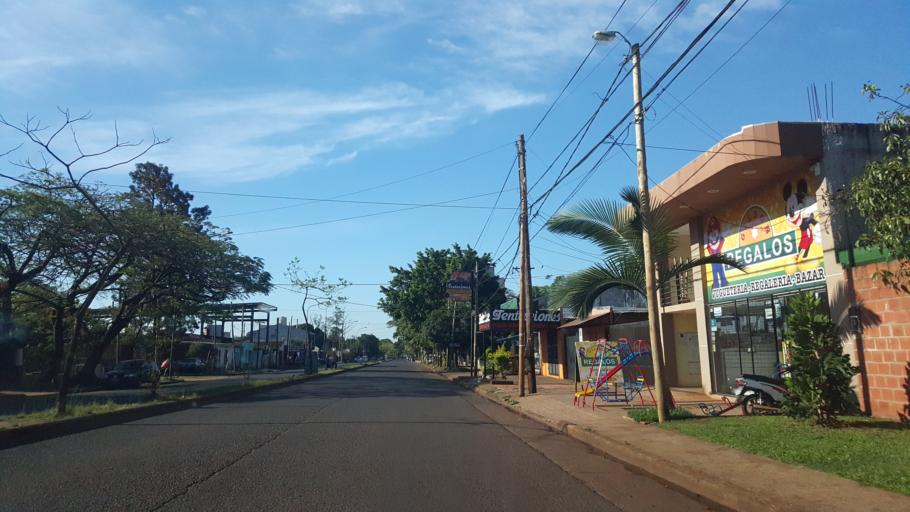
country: AR
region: Misiones
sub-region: Departamento de Capital
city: Posadas
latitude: -27.3804
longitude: -55.9183
